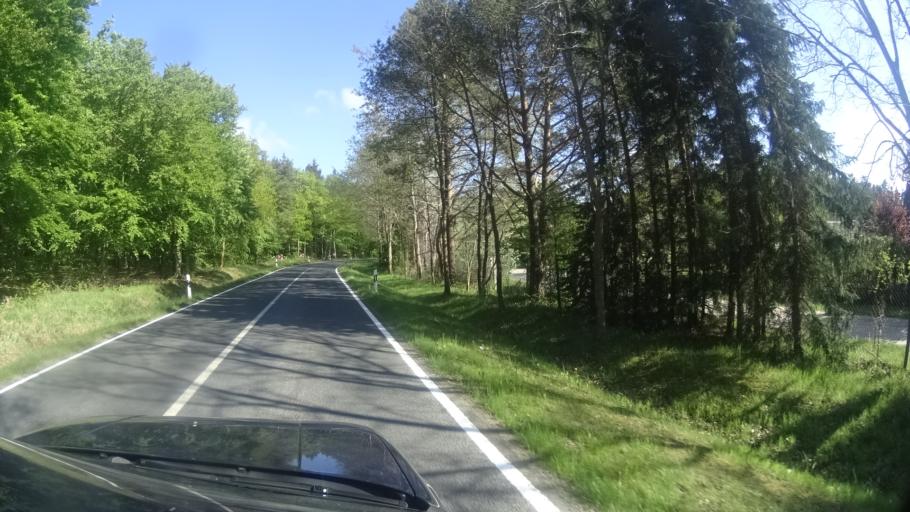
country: DE
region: Mecklenburg-Vorpommern
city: Gelbensande
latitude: 54.2533
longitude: 12.3092
